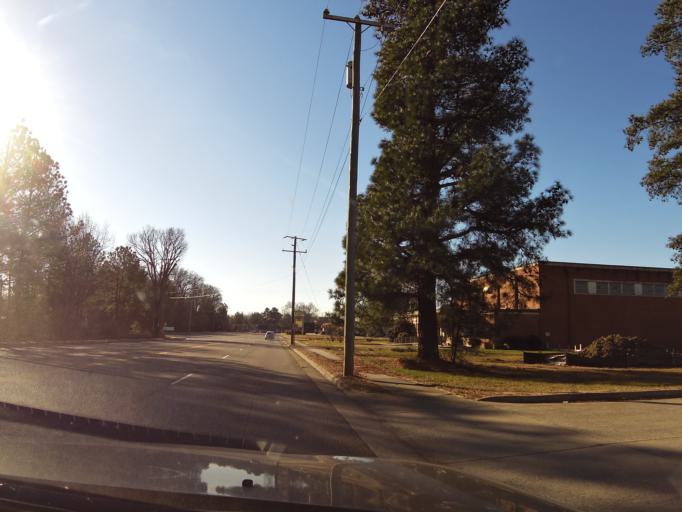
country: US
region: Virginia
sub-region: City of Hopewell
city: Hopewell
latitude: 37.2961
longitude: -77.2903
